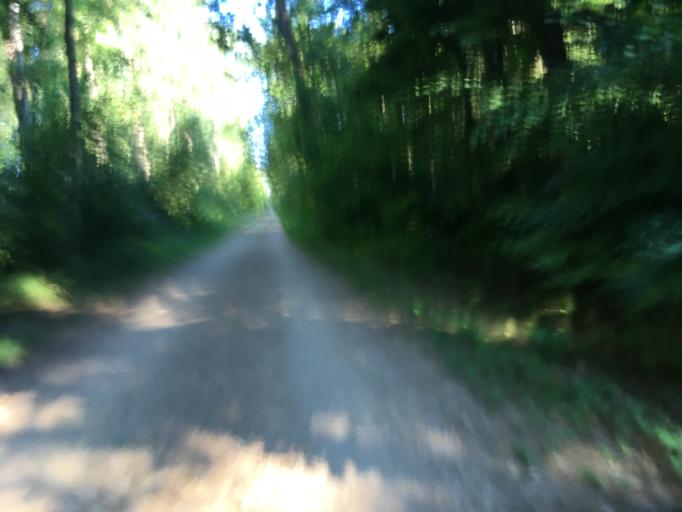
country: CH
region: Fribourg
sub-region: See District
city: Bas-Vully
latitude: 46.9598
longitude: 7.1220
